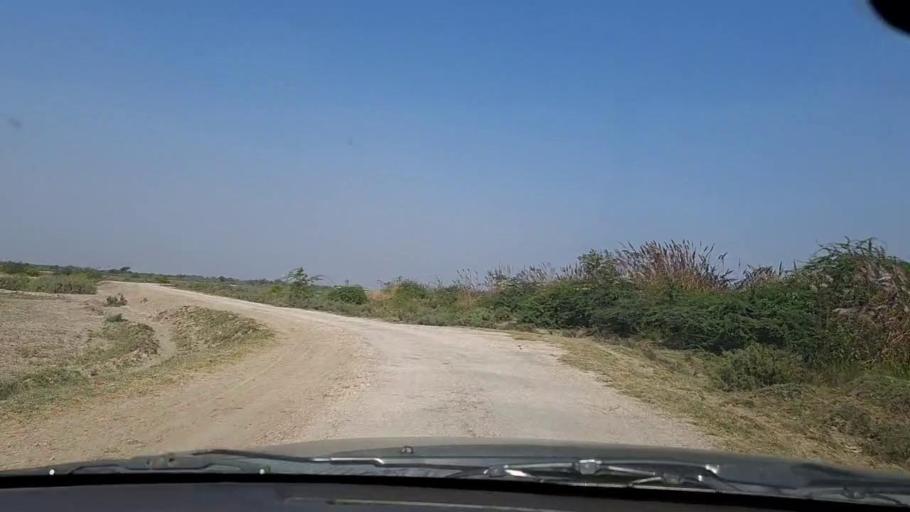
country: PK
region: Sindh
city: Chuhar Jamali
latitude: 24.4324
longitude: 67.7998
